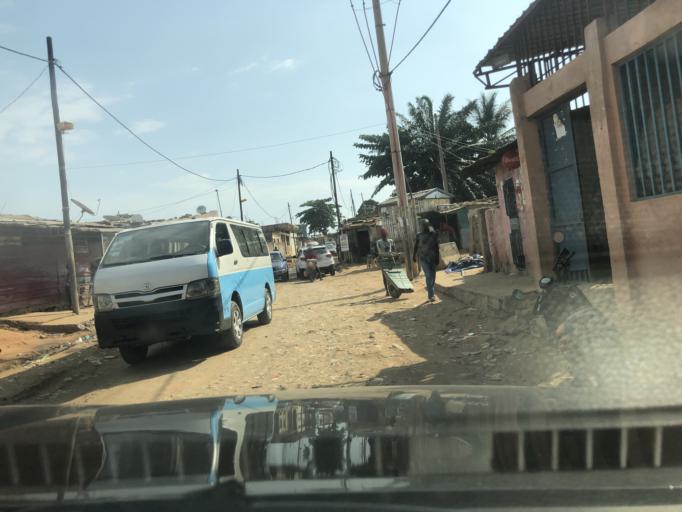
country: AO
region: Luanda
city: Luanda
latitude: -8.8523
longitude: 13.2563
